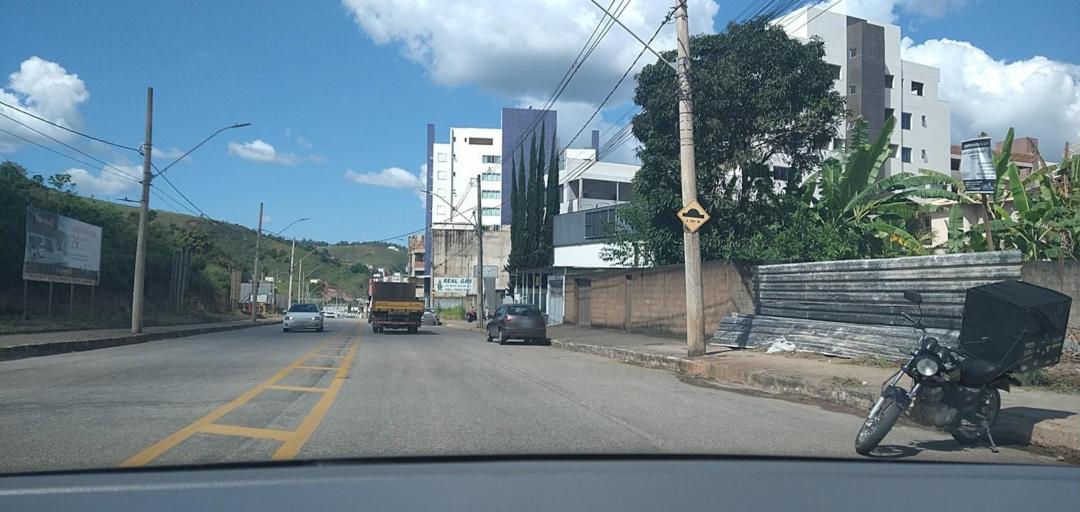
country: BR
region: Minas Gerais
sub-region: Joao Monlevade
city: Joao Monlevade
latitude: -19.8111
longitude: -43.1898
